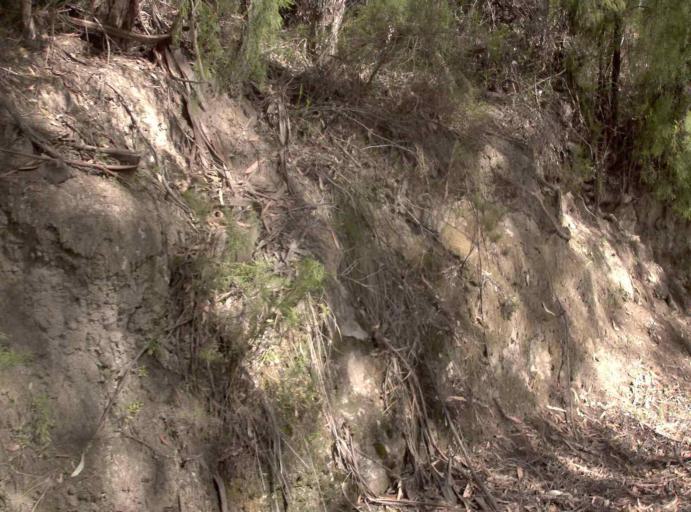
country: AU
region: Victoria
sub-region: East Gippsland
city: Lakes Entrance
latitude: -37.4165
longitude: 148.1220
